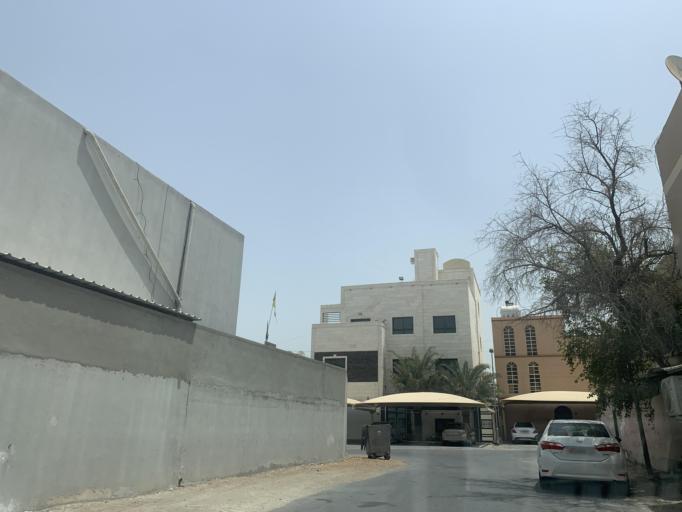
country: BH
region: Northern
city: Madinat `Isa
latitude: 26.1550
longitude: 50.5227
